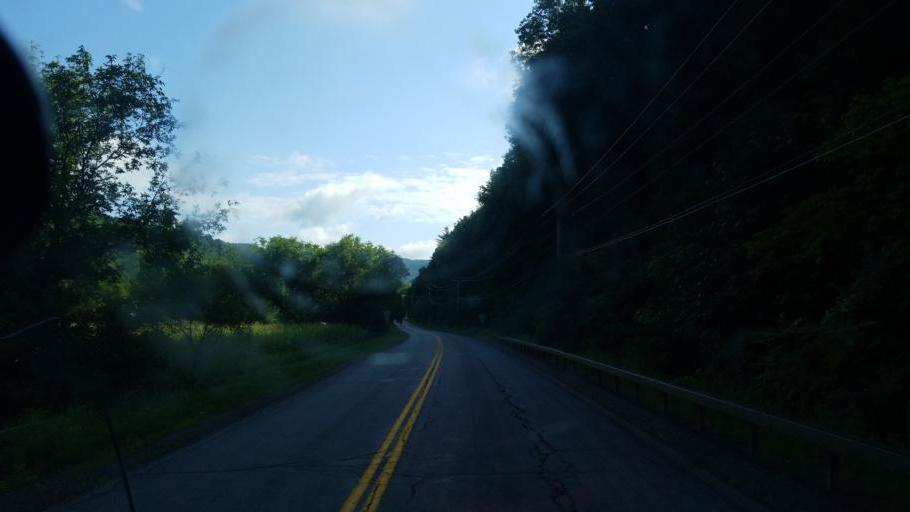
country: US
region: New York
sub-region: Steuben County
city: Canisteo
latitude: 42.2583
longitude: -77.6245
